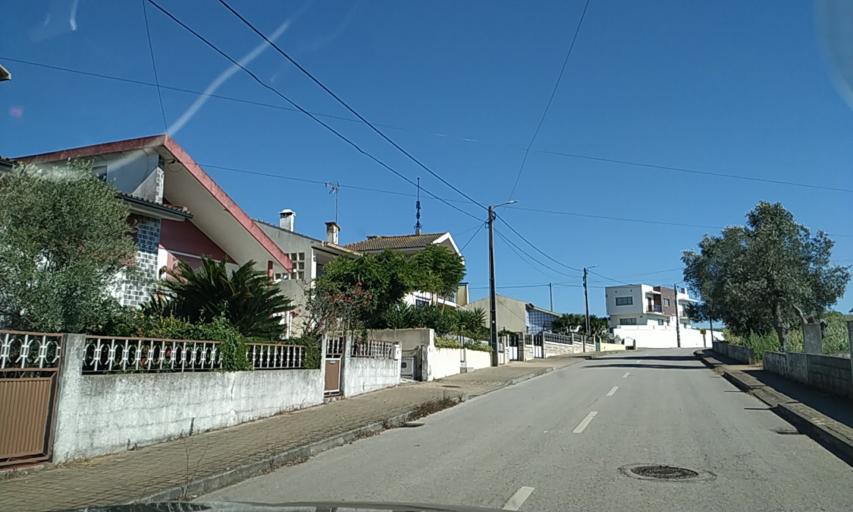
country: PT
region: Aveiro
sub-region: Estarreja
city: Salreu
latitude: 40.7455
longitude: -8.5469
